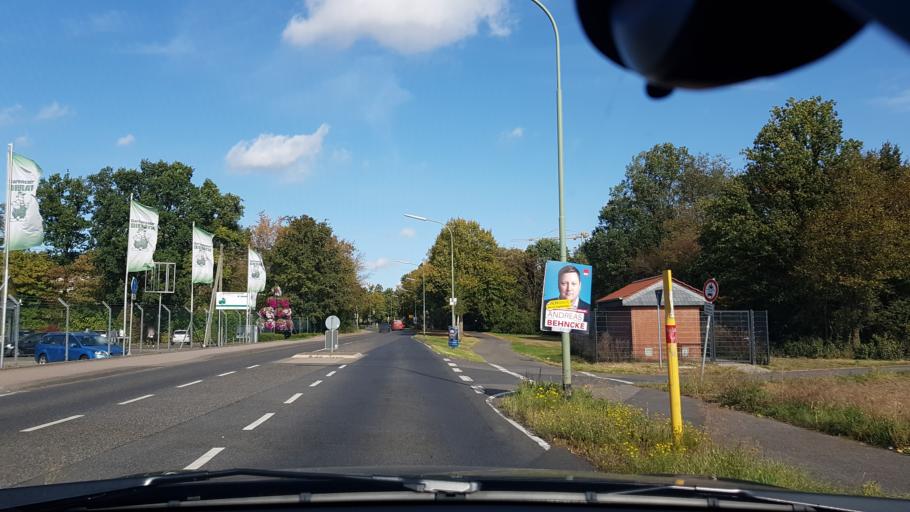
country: DE
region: North Rhine-Westphalia
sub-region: Regierungsbezirk Dusseldorf
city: Neuss
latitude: 51.1503
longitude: 6.6991
